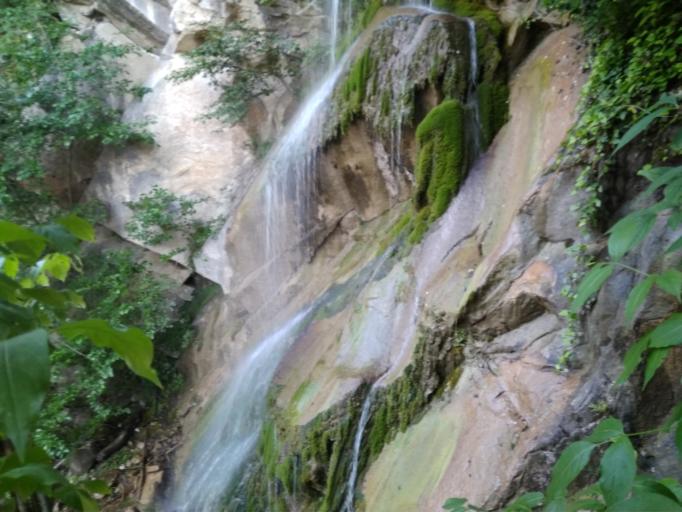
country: RU
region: Krasnodarskiy
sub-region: Sochi City
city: Lazarevskoye
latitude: 43.9989
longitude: 39.3969
